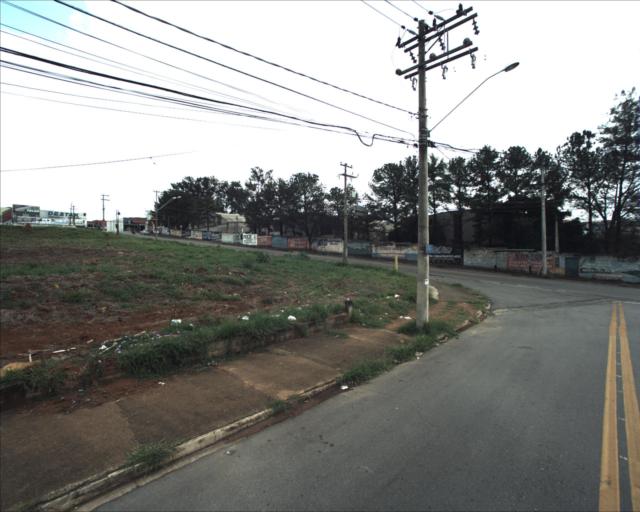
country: BR
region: Sao Paulo
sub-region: Sorocaba
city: Sorocaba
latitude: -23.4430
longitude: -47.4774
